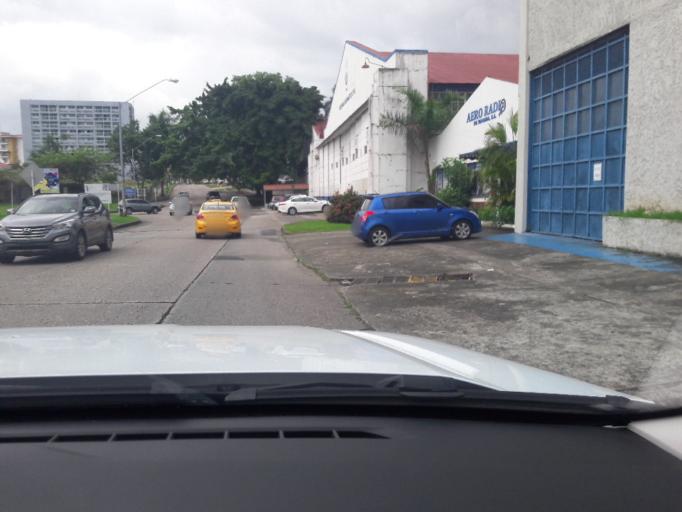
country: PA
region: Panama
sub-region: Distrito de Panama
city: Ancon
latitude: 8.9737
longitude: -79.5588
